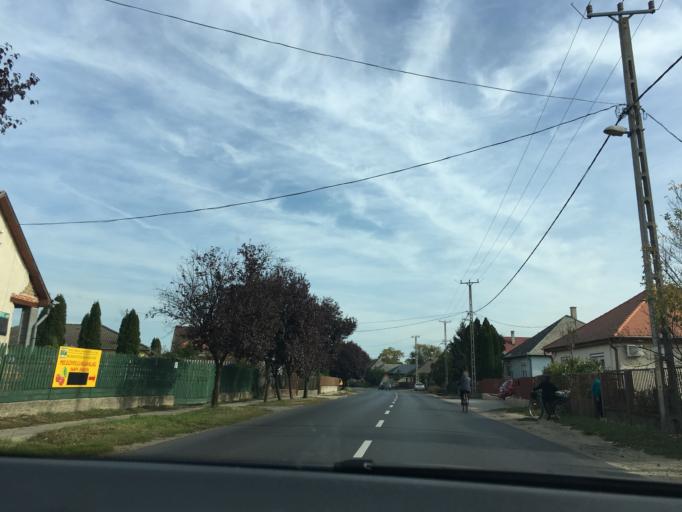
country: HU
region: Szabolcs-Szatmar-Bereg
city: Kallosemjen
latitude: 47.8591
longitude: 21.9178
